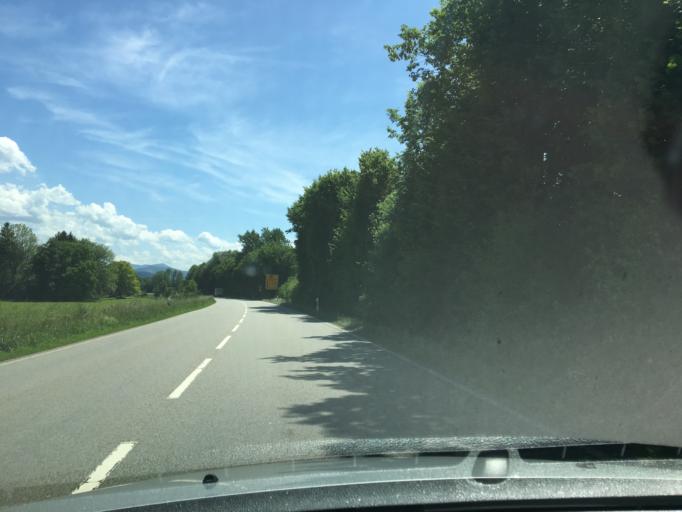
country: DE
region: Bavaria
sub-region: Upper Bavaria
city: Freilassing
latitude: 47.8574
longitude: 12.9834
